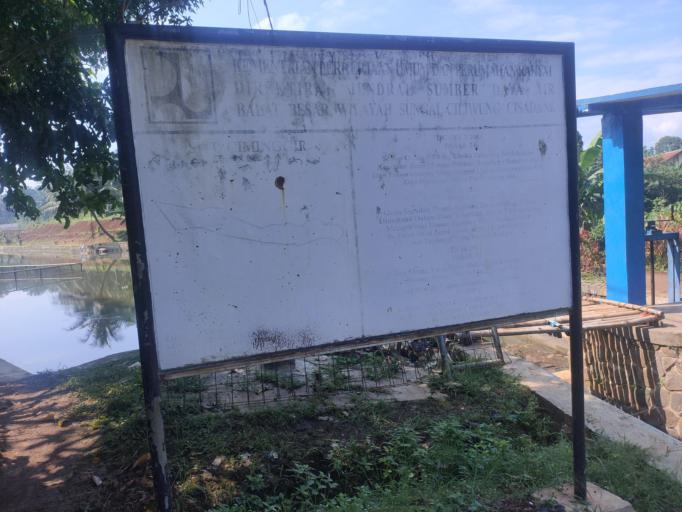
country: ID
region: West Java
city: Ciampea
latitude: -6.5225
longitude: 106.7058
